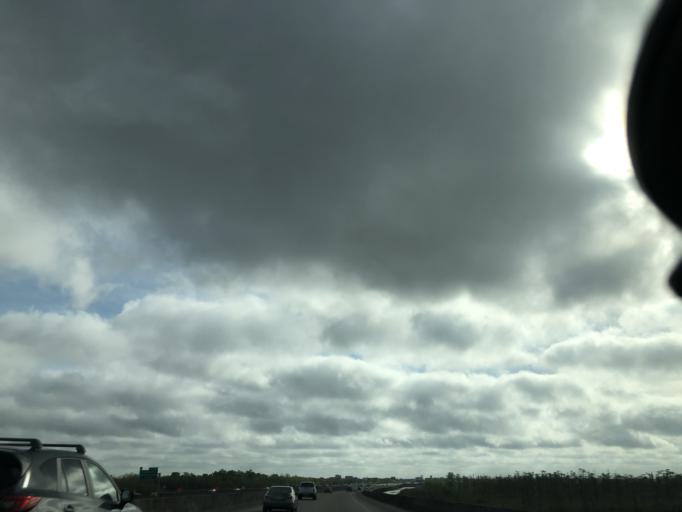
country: US
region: Louisiana
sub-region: Jefferson Parish
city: Kenner
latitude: 30.0051
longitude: -90.2890
